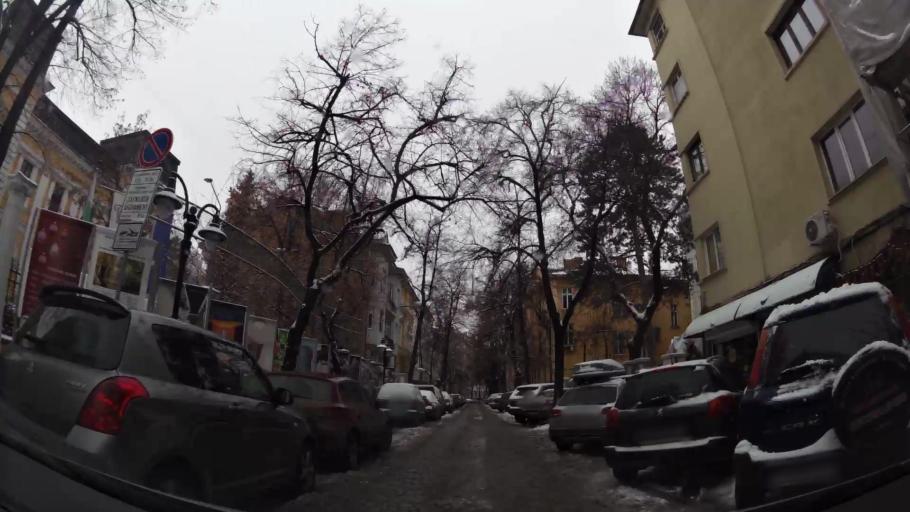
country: BG
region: Sofia-Capital
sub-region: Stolichna Obshtina
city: Sofia
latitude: 42.6936
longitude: 23.3371
